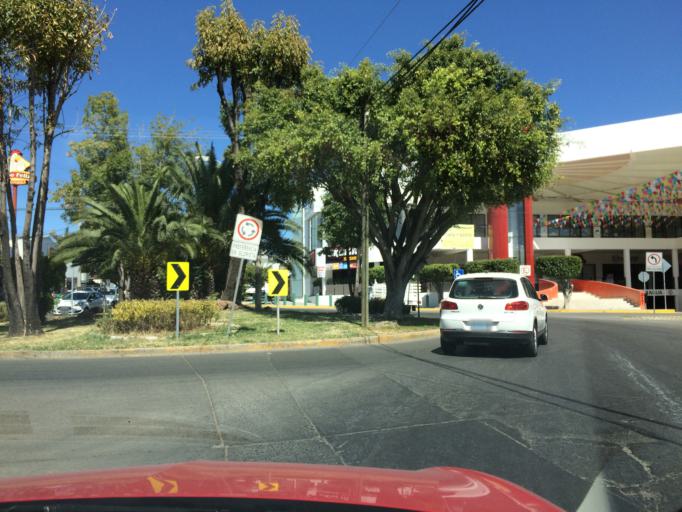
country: MX
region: Guanajuato
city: Leon
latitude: 21.1182
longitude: -101.6955
